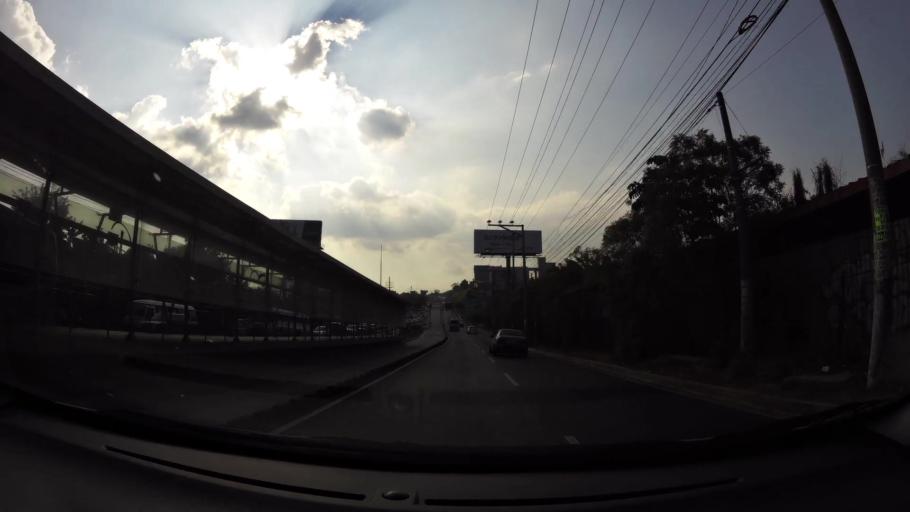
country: SV
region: San Salvador
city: Delgado
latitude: 13.7012
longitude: -89.1648
